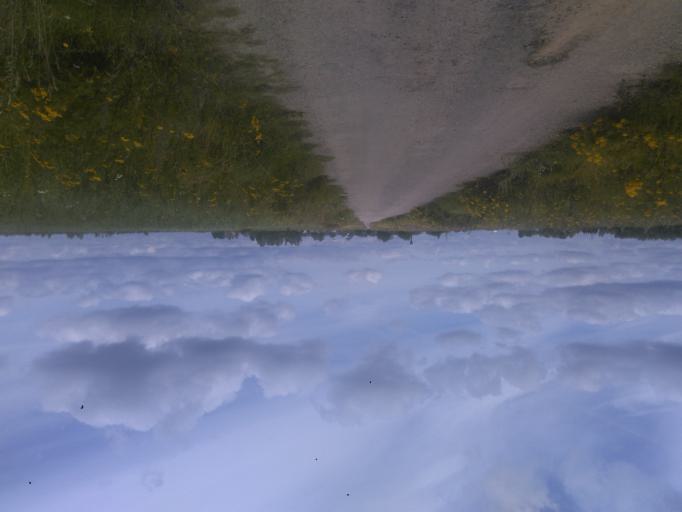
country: RU
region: Moskovskaya
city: Solnechnogorsk
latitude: 56.1408
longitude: 36.9280
